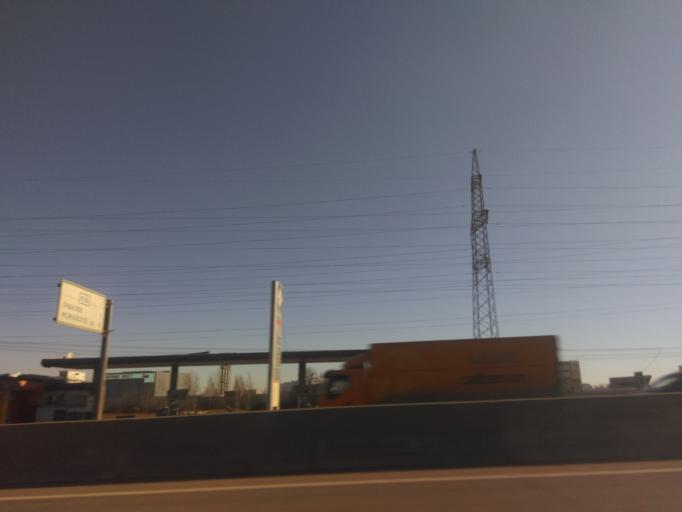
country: RU
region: Moscow
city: Mikhalkovo
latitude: 55.6716
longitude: 37.4249
